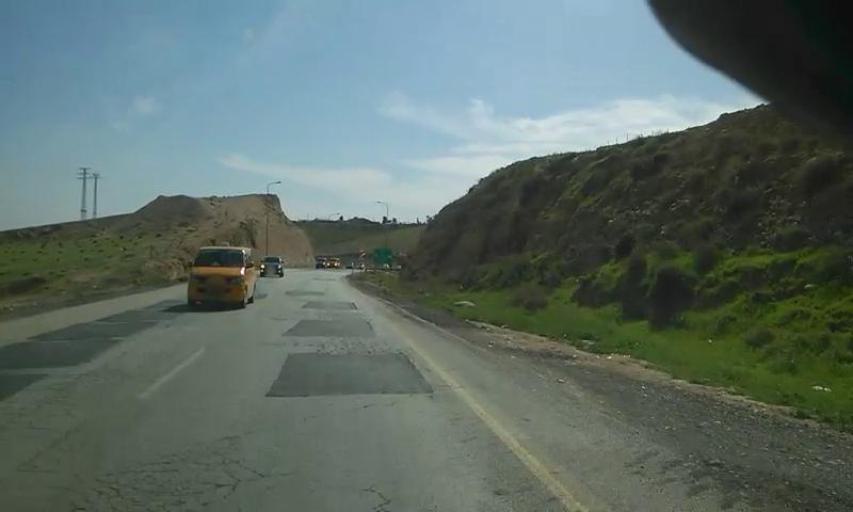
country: PS
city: Az Za`ayyim
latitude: 31.8069
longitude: 35.3240
